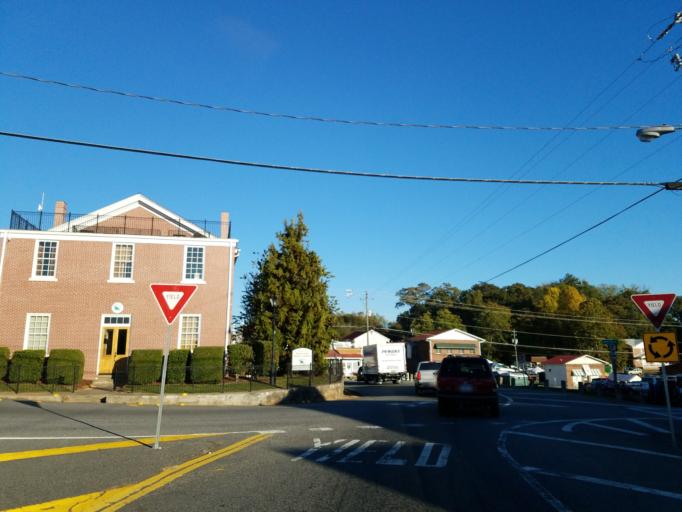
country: US
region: Georgia
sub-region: Dawson County
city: Dawsonville
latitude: 34.4213
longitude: -84.1195
